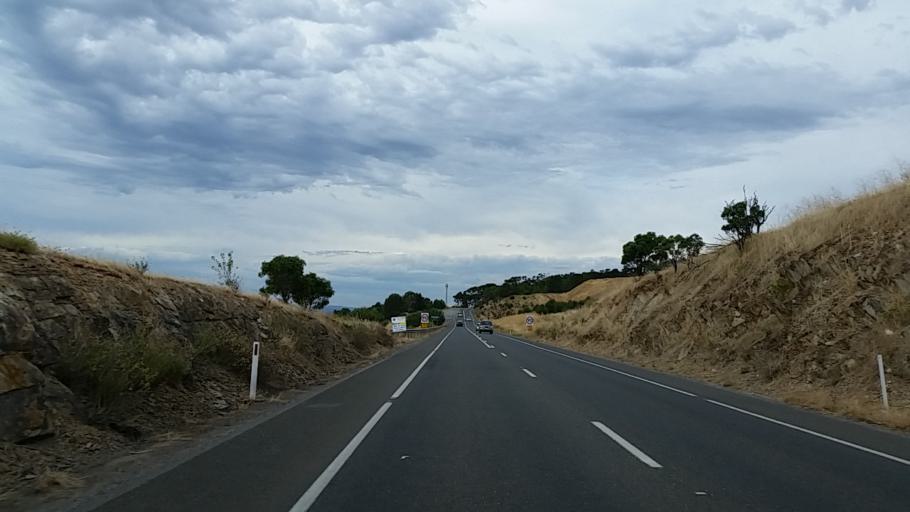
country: AU
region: South Australia
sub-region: Onkaparinga
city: Aldinga
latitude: -35.3426
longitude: 138.4600
